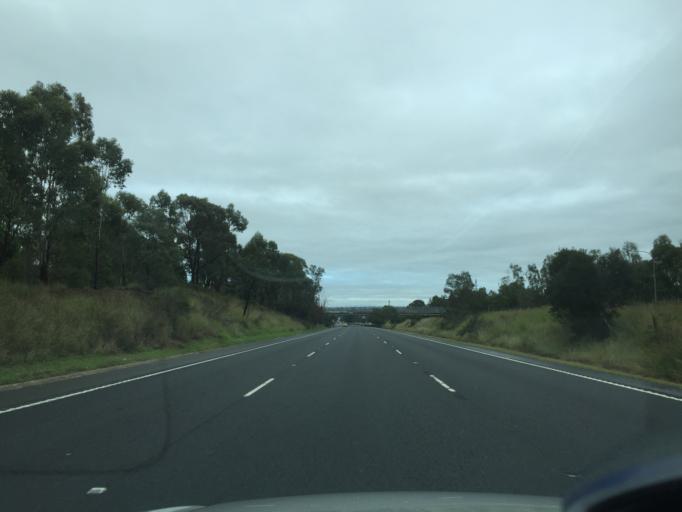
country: AU
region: New South Wales
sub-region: Blacktown
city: Mount Druitt
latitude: -33.7847
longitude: 150.7742
